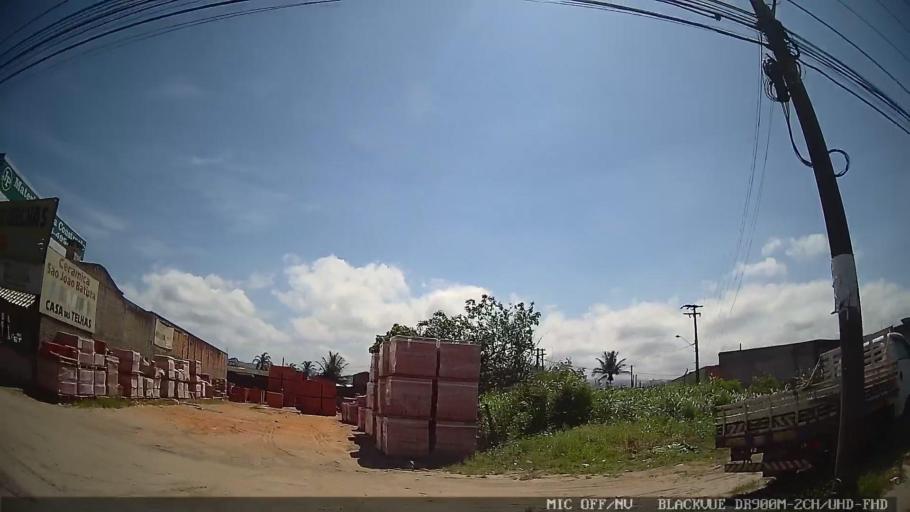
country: BR
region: Sao Paulo
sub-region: Peruibe
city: Peruibe
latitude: -24.3016
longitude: -46.9877
